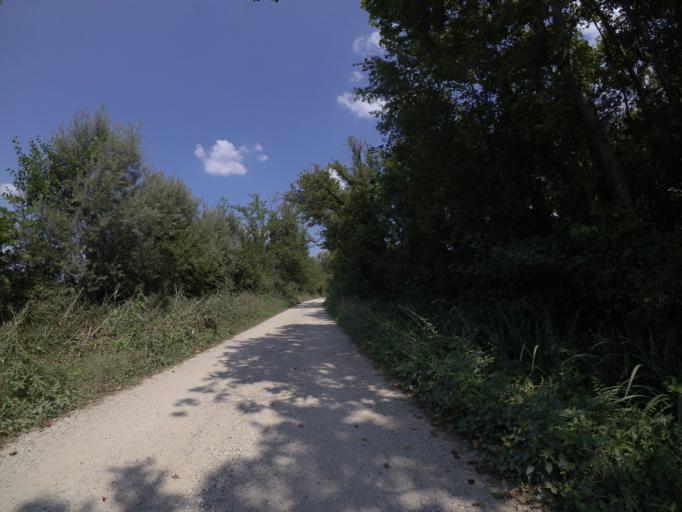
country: IT
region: Friuli Venezia Giulia
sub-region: Provincia di Udine
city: Bertiolo
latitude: 45.9233
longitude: 13.0744
